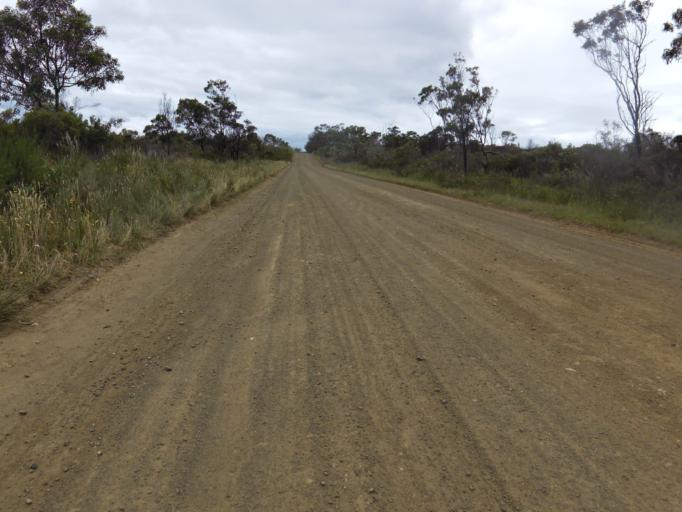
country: AU
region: Victoria
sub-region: Bass Coast
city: Cowes
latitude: -38.3824
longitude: 145.2860
